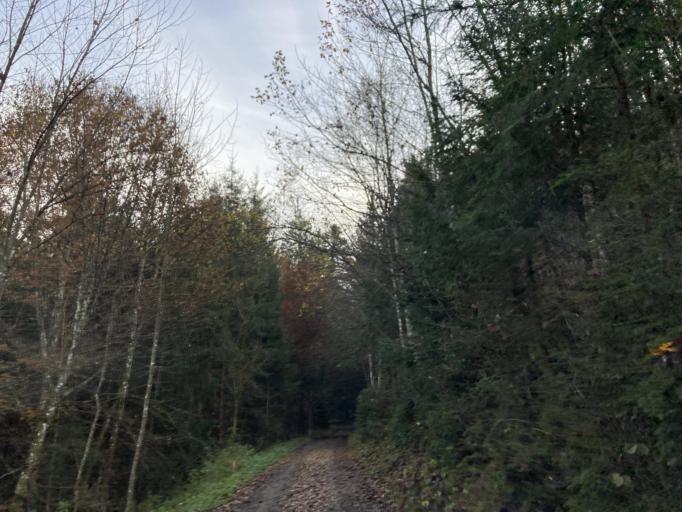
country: DE
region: Baden-Wuerttemberg
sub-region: Regierungsbezirk Stuttgart
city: Bondorf
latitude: 48.4660
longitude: 8.8526
